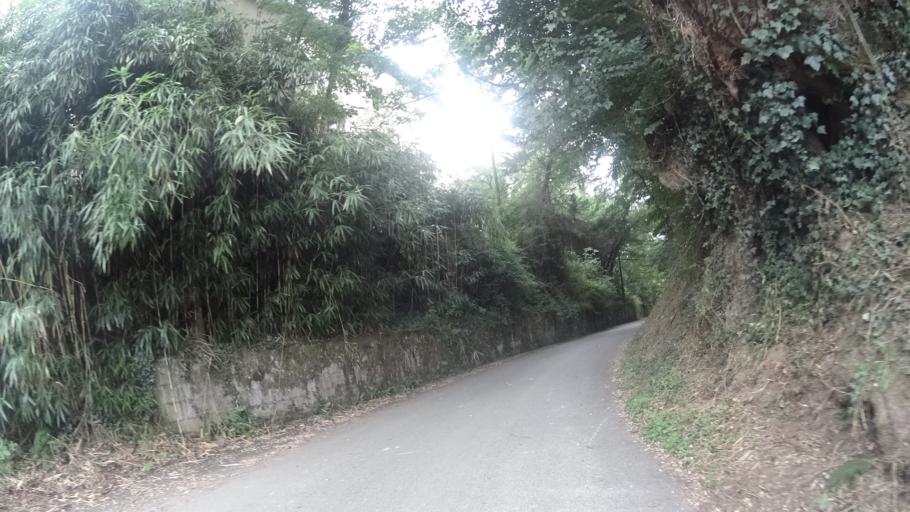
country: FR
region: Aquitaine
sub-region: Departement des Pyrenees-Atlantiques
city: Orthez
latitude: 43.4683
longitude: -0.7161
